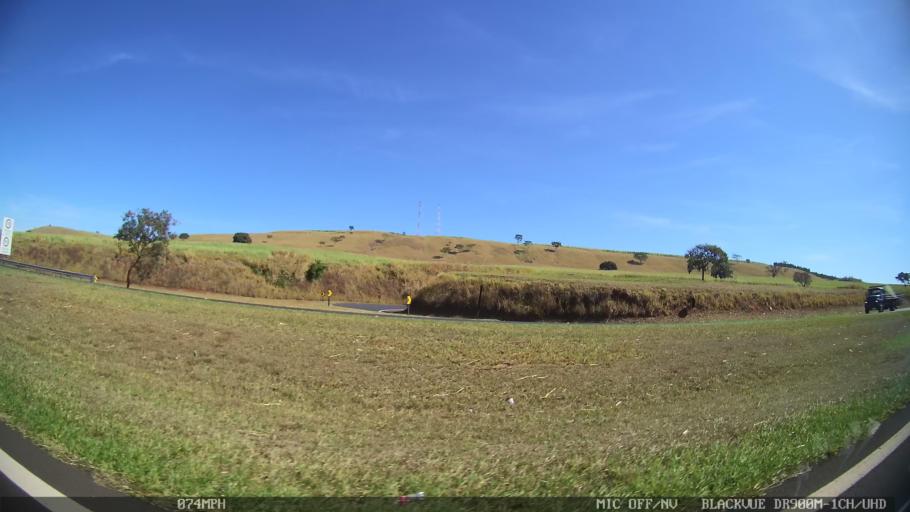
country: BR
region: Sao Paulo
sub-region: Sao Simao
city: Sao Simao
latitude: -21.4685
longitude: -47.6411
